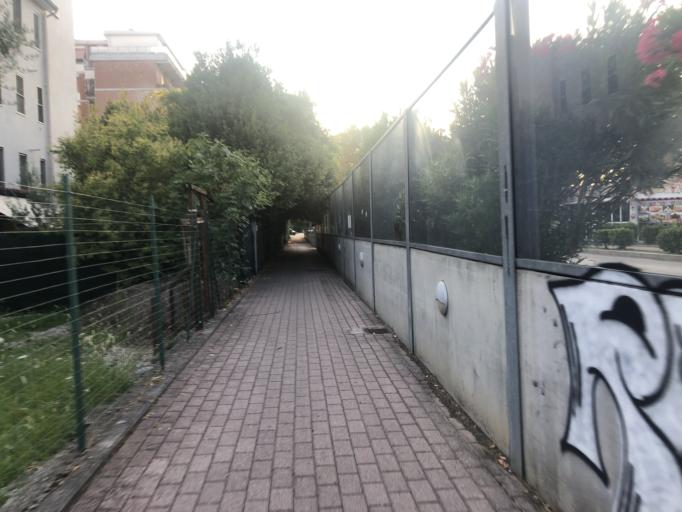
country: IT
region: Tuscany
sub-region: Province of Pisa
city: Pisa
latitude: 43.7242
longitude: 10.4105
